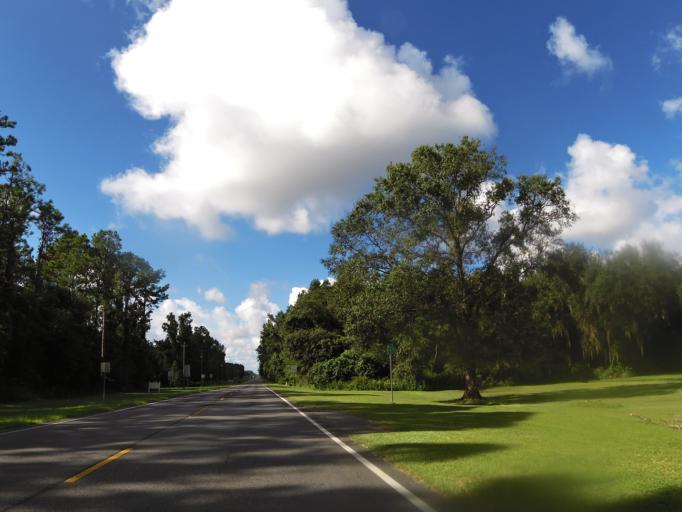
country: US
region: Georgia
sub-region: Camden County
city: Kingsland
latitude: 30.8132
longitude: -81.6927
